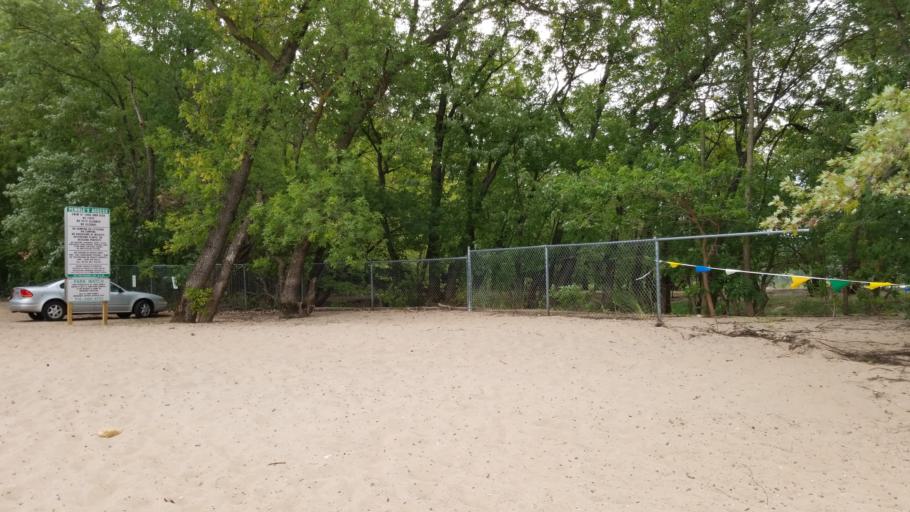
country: US
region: Minnesota
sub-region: Washington County
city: Afton
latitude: 44.8821
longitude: -92.7647
